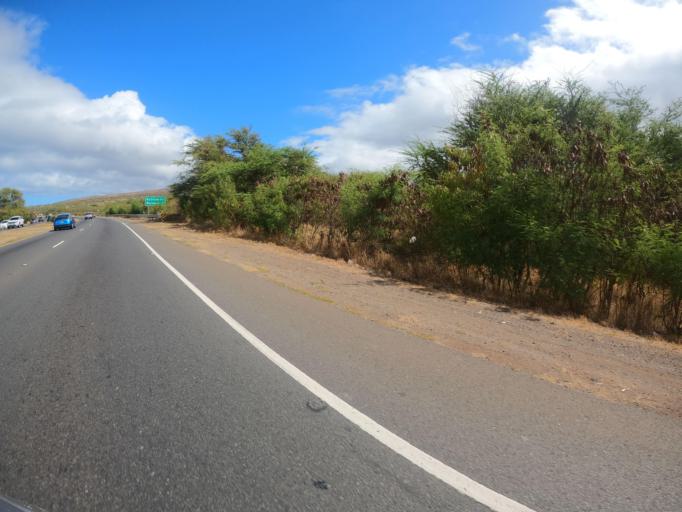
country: US
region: Hawaii
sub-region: Honolulu County
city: Makakilo City
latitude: 21.3354
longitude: -158.0947
